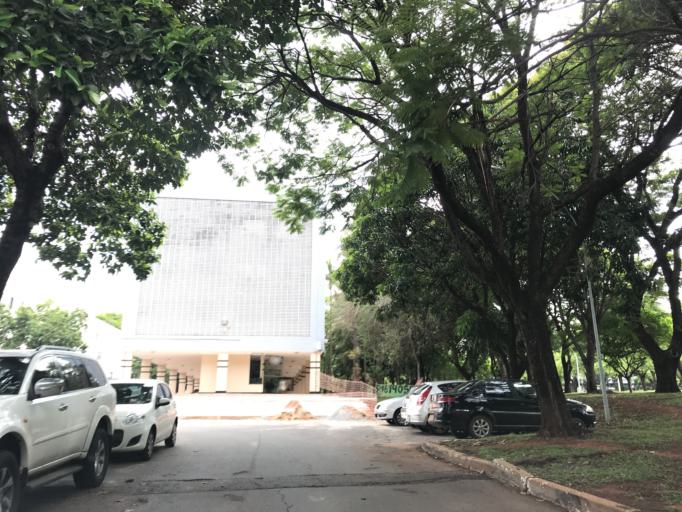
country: BR
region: Federal District
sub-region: Brasilia
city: Brasilia
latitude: -15.8071
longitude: -47.8852
